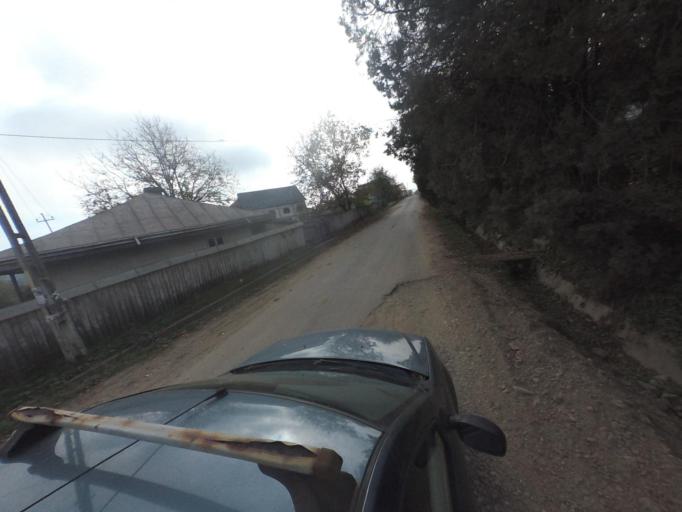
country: RO
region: Vaslui
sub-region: Comuna Bacesti
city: Bacesti
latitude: 46.8256
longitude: 27.2442
